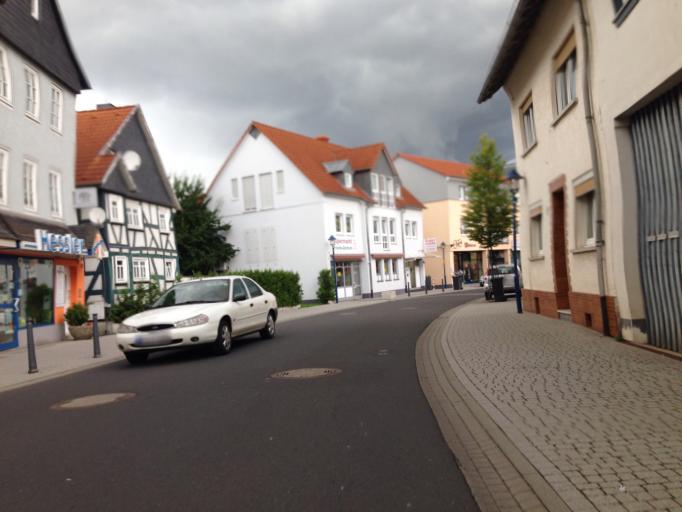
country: DE
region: Hesse
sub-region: Regierungsbezirk Giessen
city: Hungen
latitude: 50.4762
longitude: 8.9016
